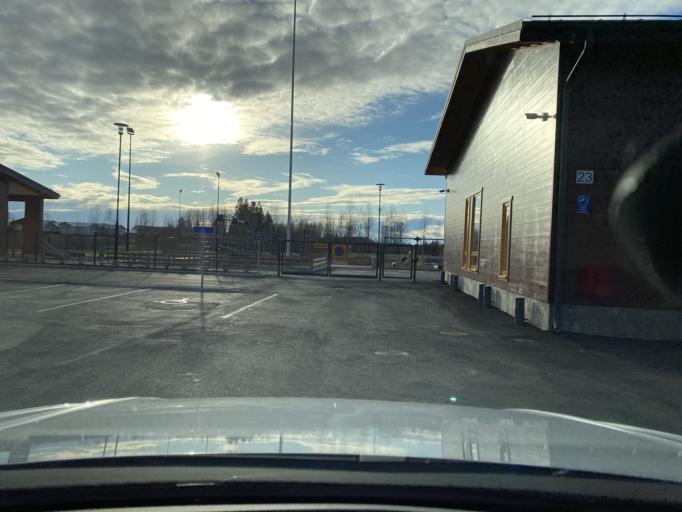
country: FI
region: Pirkanmaa
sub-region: Lounais-Pirkanmaa
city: Punkalaidun
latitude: 61.1191
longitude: 23.1139
